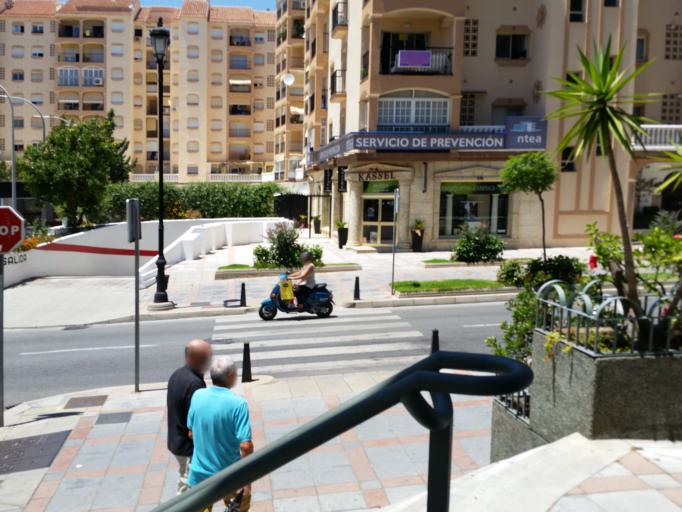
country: ES
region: Andalusia
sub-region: Provincia de Malaga
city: Fuengirola
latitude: 36.5479
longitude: -4.6181
